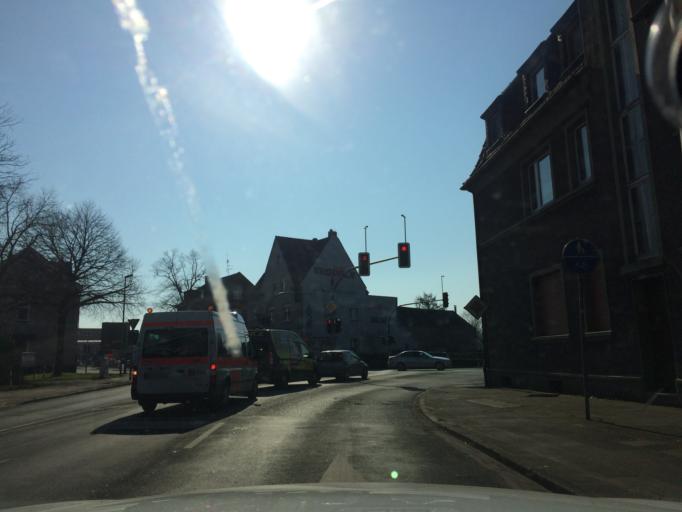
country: DE
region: North Rhine-Westphalia
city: Herten
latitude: 51.5998
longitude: 7.0943
